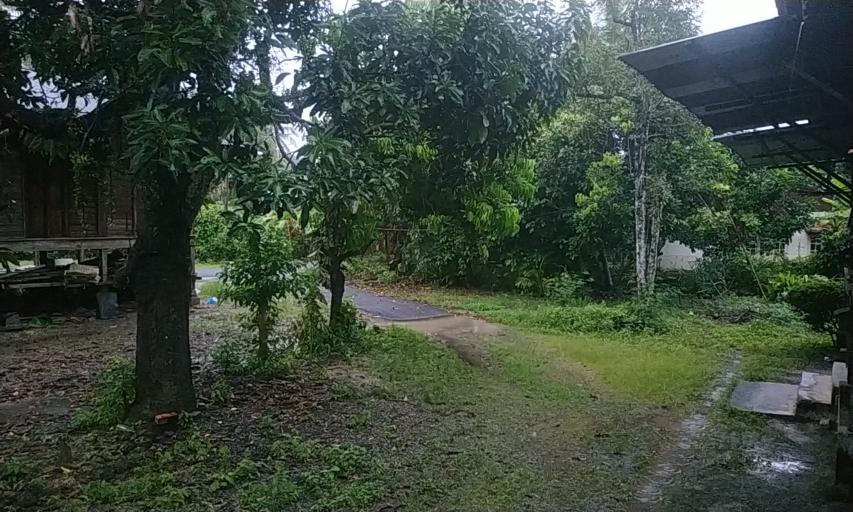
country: MY
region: Kedah
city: Jitra
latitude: 6.2866
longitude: 100.4382
